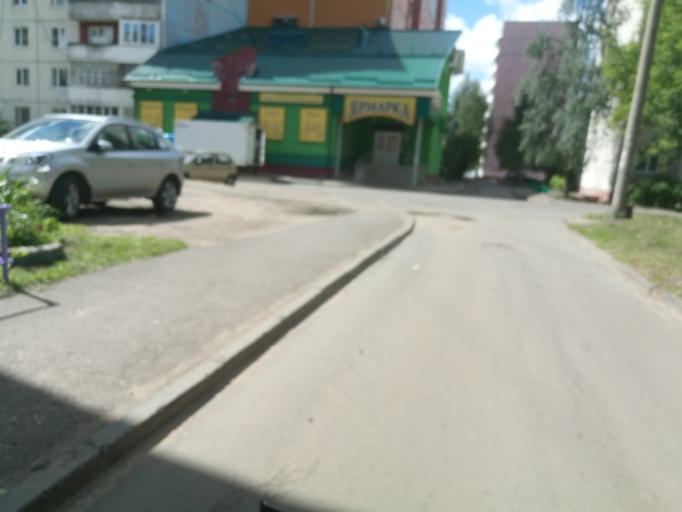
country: RU
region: Jaroslavl
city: Yaroslavl
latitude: 57.6521
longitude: 39.9627
